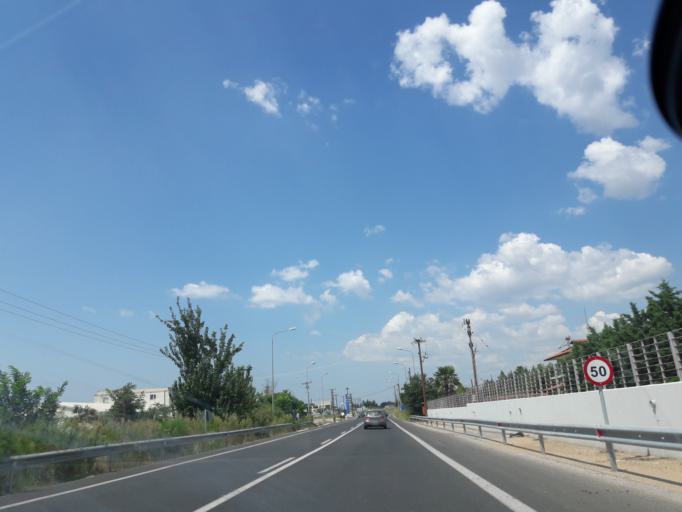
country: GR
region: Central Macedonia
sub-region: Nomos Thessalonikis
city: Agia Paraskevi
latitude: 40.5163
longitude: 23.0684
